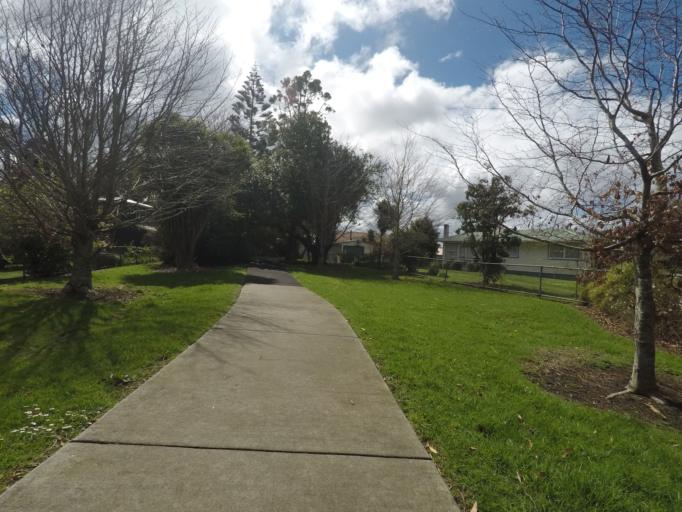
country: NZ
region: Auckland
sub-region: Auckland
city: Rosebank
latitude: -36.8877
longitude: 174.6746
